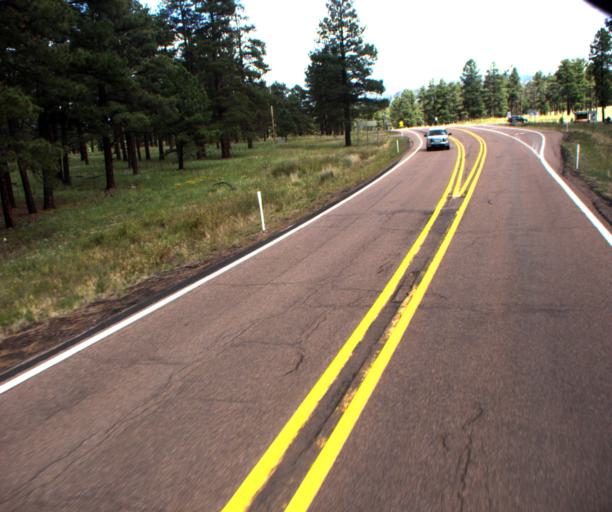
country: US
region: Arizona
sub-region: Apache County
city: Eagar
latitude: 34.0762
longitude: -109.4686
